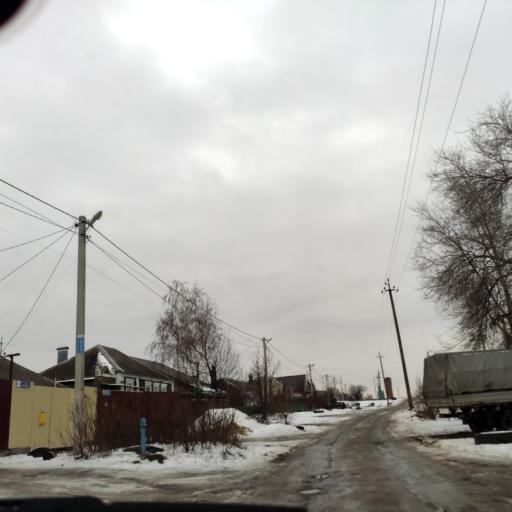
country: RU
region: Voronezj
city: Pridonskoy
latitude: 51.7023
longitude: 39.0710
